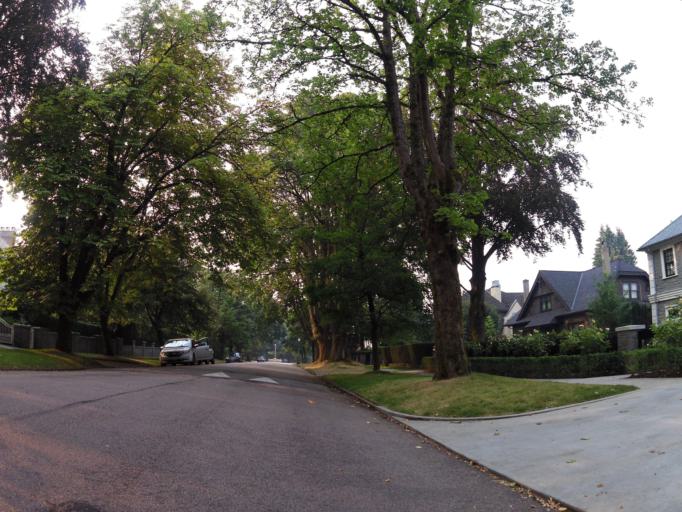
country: CA
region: British Columbia
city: Vancouver
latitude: 49.2489
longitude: -123.1462
